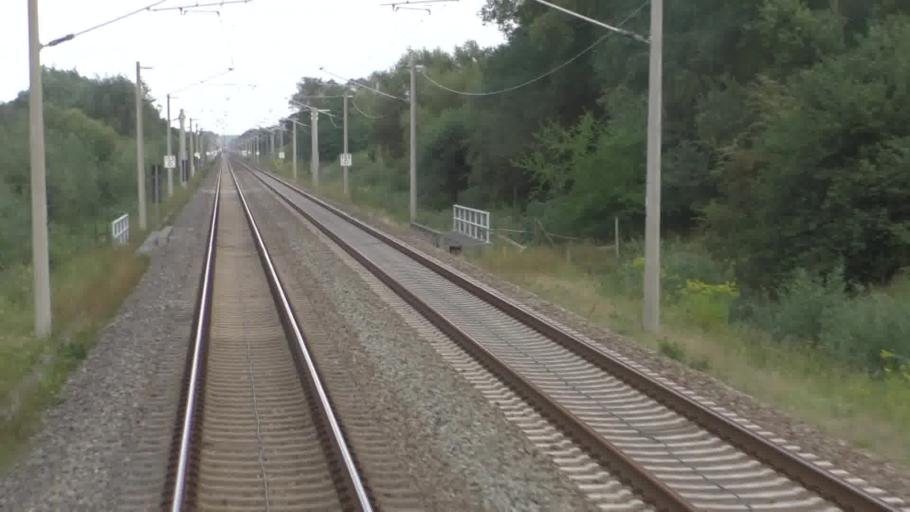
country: DE
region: Brandenburg
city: Kotzen
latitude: 52.5948
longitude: 12.5858
